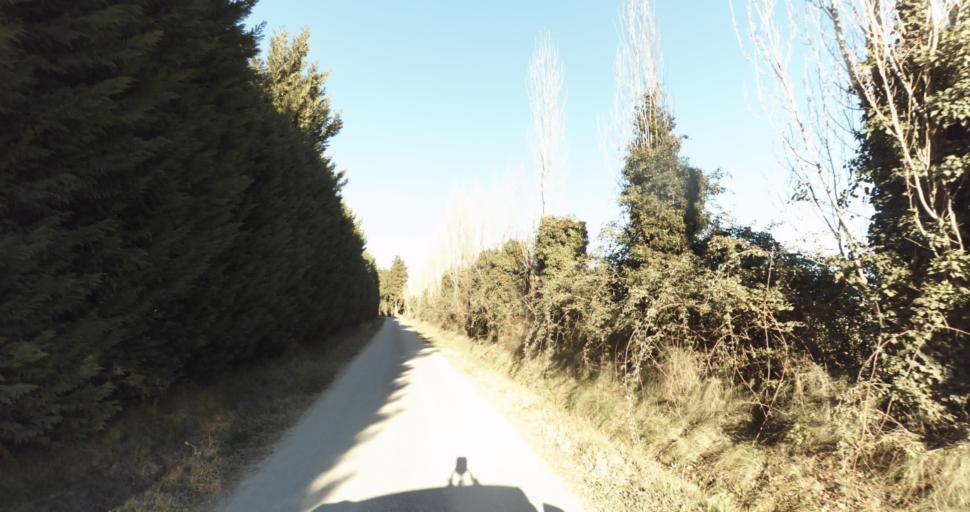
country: FR
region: Provence-Alpes-Cote d'Azur
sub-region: Departement des Bouches-du-Rhone
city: Barbentane
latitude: 43.9027
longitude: 4.7457
